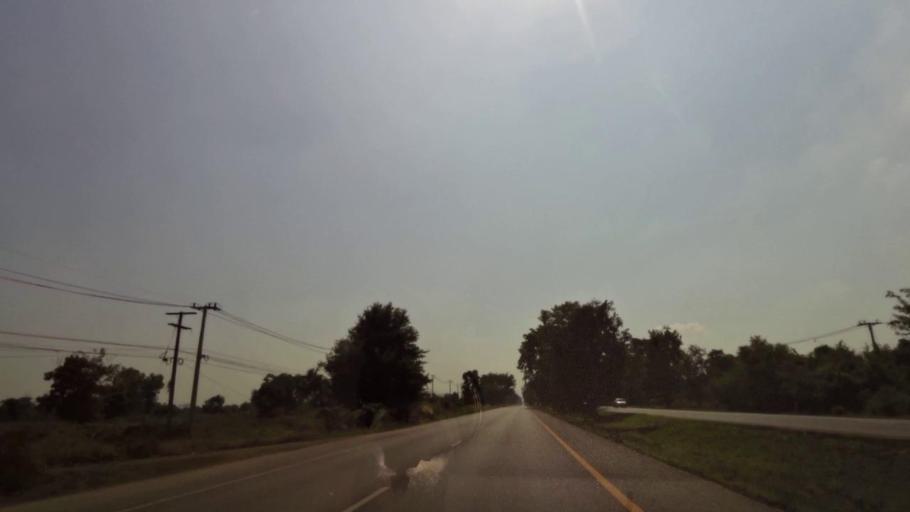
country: TH
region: Phichit
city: Bueng Na Rang
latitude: 16.2910
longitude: 100.1282
